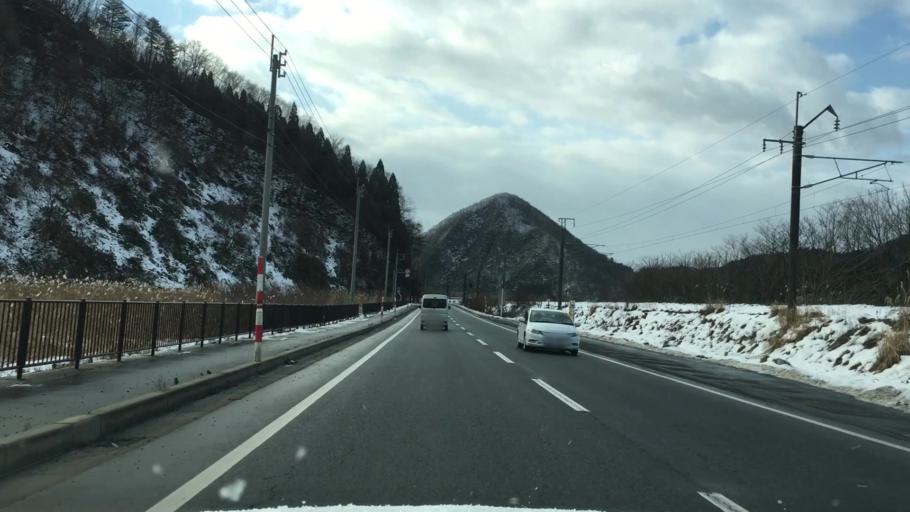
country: JP
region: Akita
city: Odate
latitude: 40.3686
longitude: 140.5990
